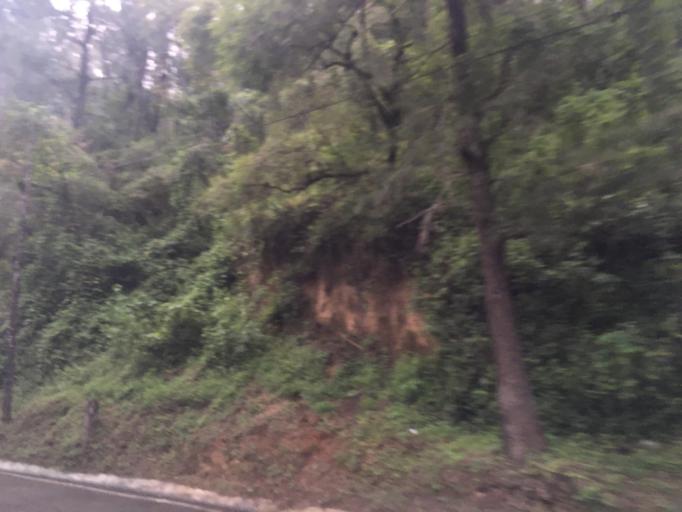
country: GT
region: Sacatepequez
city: Antigua Guatemala
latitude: 14.5684
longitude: -90.7270
